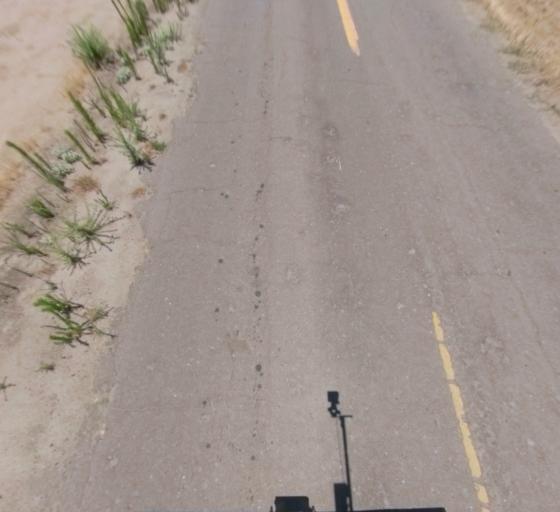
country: US
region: California
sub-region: Madera County
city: Parkwood
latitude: 36.8586
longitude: -120.0573
